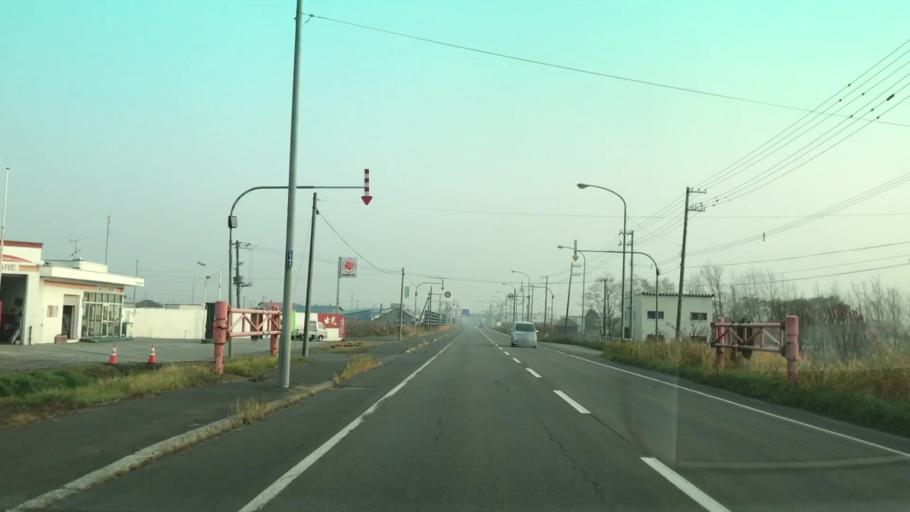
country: JP
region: Hokkaido
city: Ishikari
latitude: 43.2407
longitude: 141.3668
